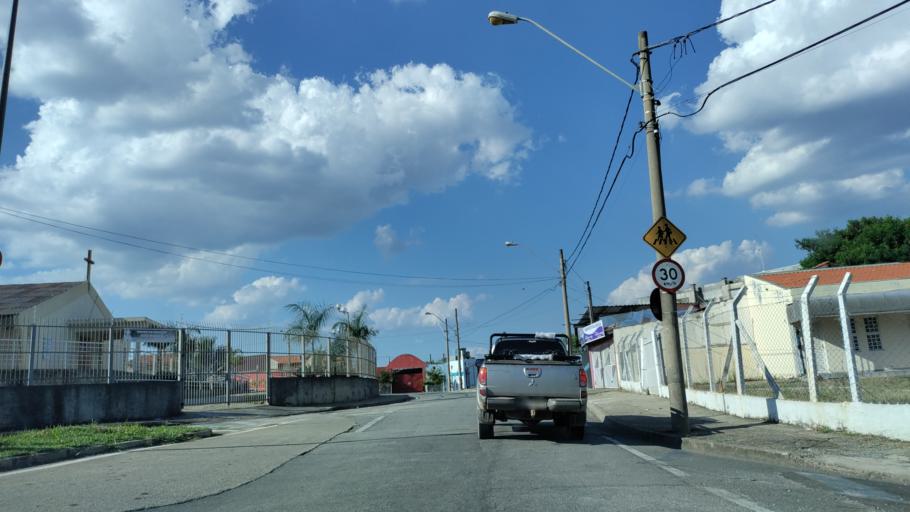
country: BR
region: Sao Paulo
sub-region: Sorocaba
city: Sorocaba
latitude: -23.4927
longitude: -47.4838
